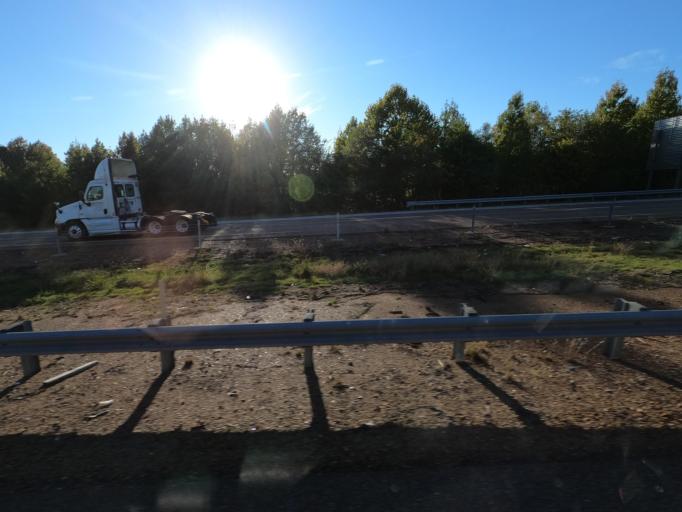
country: US
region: Tennessee
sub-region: Fayette County
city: Hickory Withe
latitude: 35.2226
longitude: -89.6560
